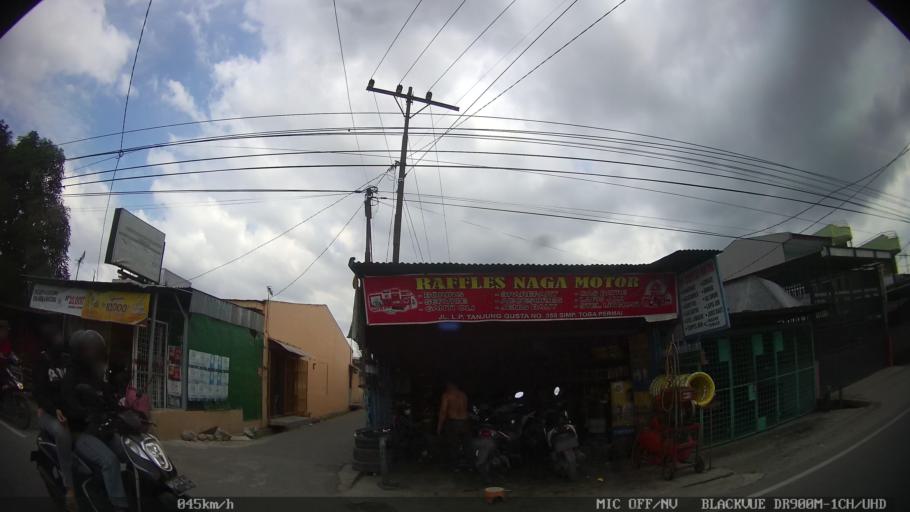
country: ID
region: North Sumatra
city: Sunggal
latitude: 3.6182
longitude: 98.6176
